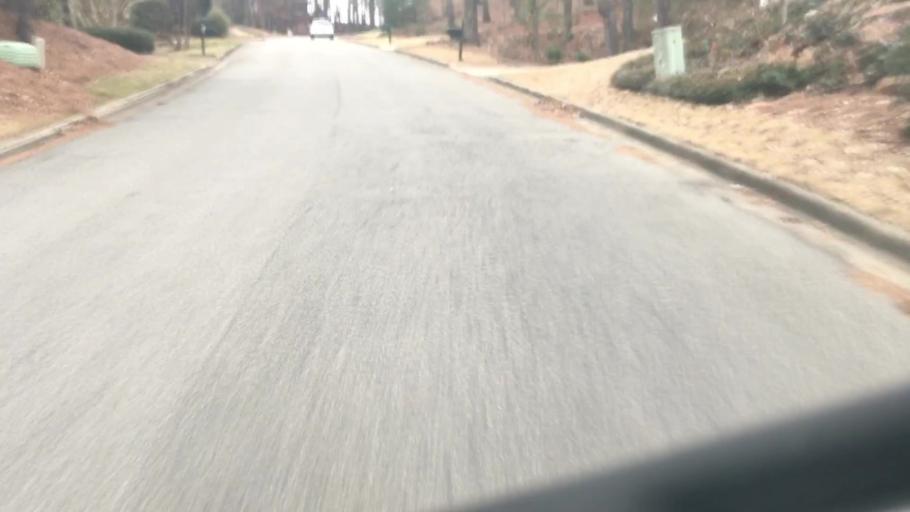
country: US
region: Alabama
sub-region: Shelby County
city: Helena
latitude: 33.3471
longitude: -86.8216
